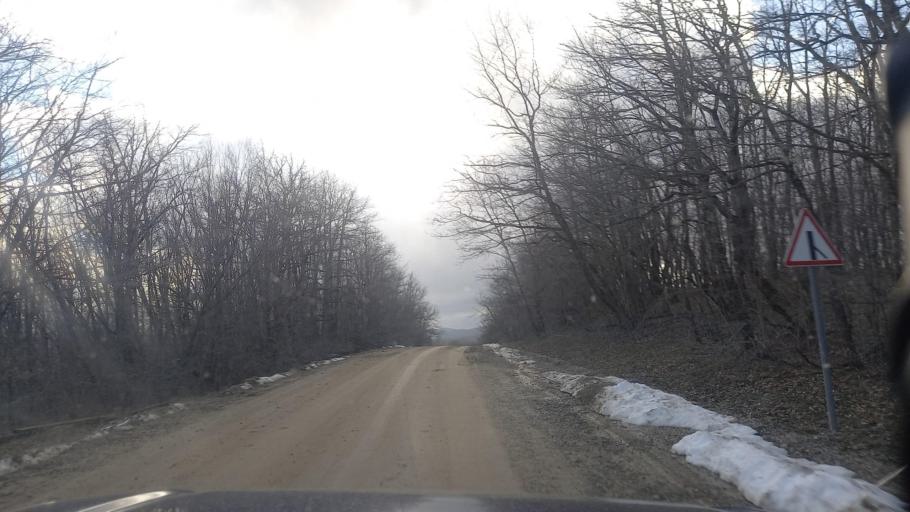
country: RU
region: Krasnodarskiy
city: Smolenskaya
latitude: 44.5768
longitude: 38.8073
